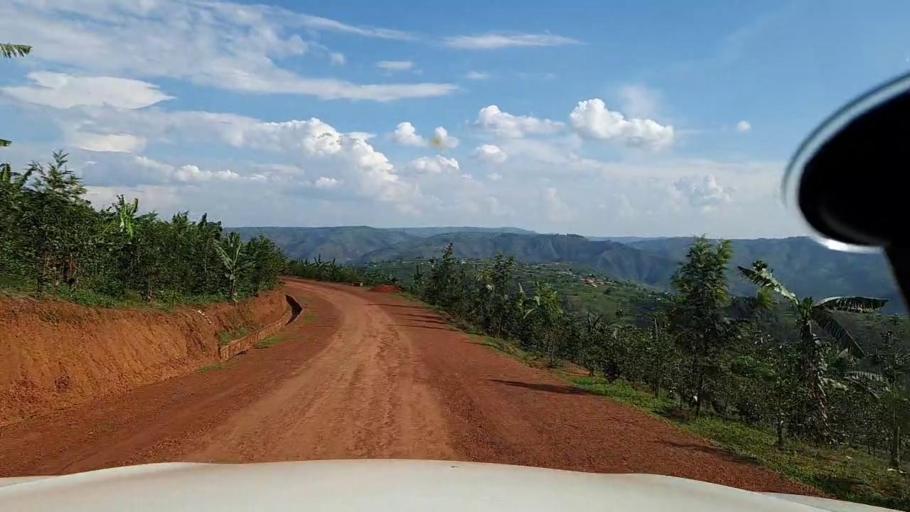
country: RW
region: Kigali
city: Kigali
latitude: -1.8365
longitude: 29.8467
